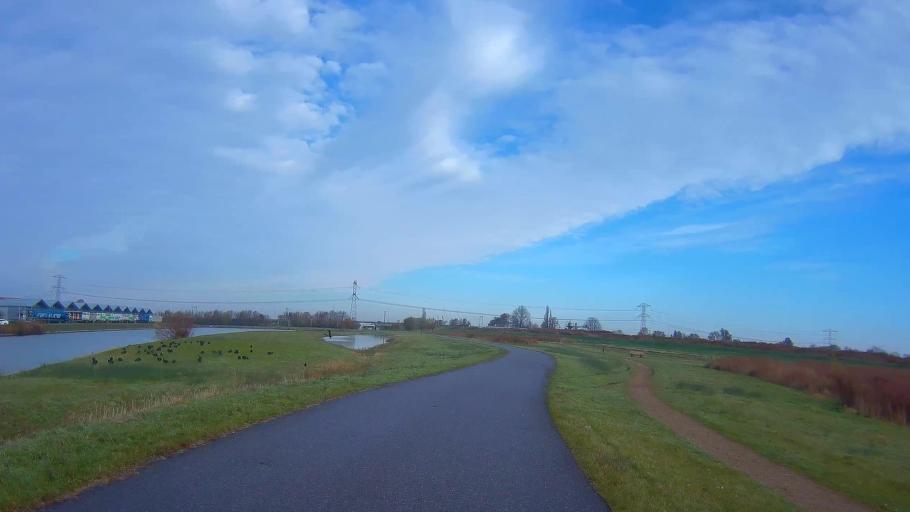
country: NL
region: South Holland
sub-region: Gemeente Lansingerland
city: Bleiswijk
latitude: 52.0279
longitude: 4.5555
